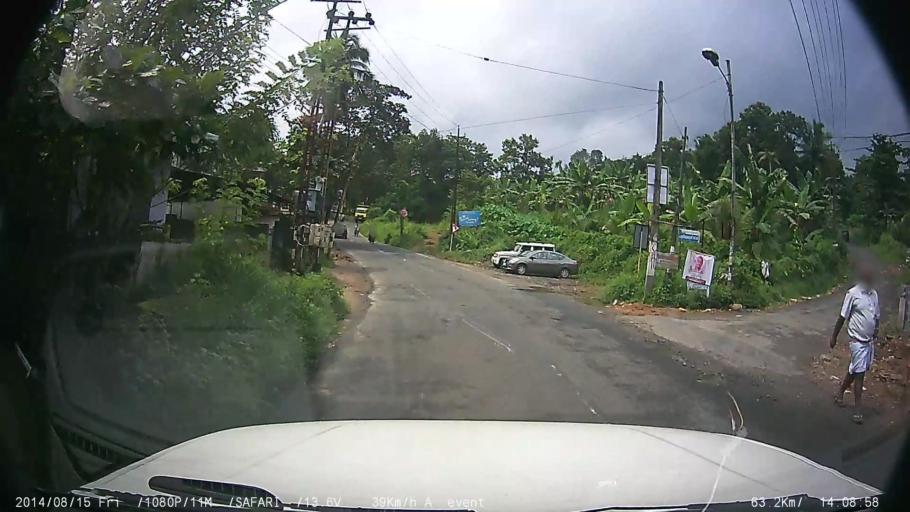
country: IN
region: Kerala
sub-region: Kottayam
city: Lalam
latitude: 9.7226
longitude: 76.6919
